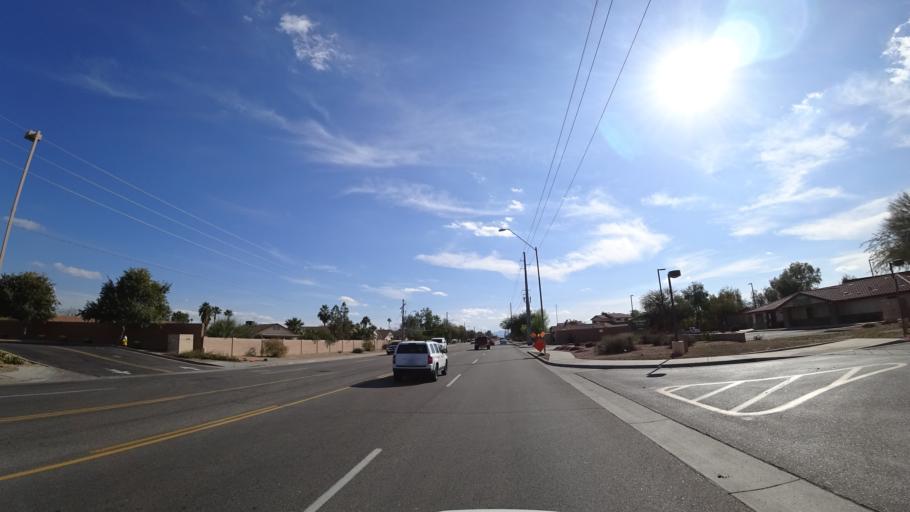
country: US
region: Arizona
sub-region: Maricopa County
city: Peoria
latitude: 33.5944
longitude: -112.2203
